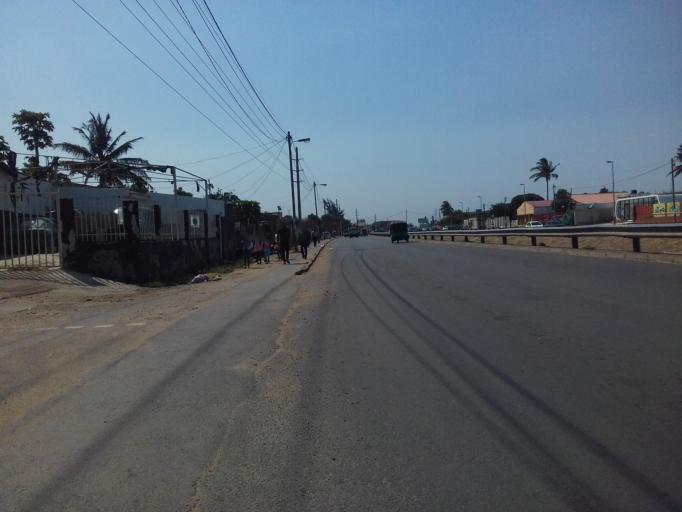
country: MZ
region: Maputo City
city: Maputo
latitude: -25.9454
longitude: 32.5752
